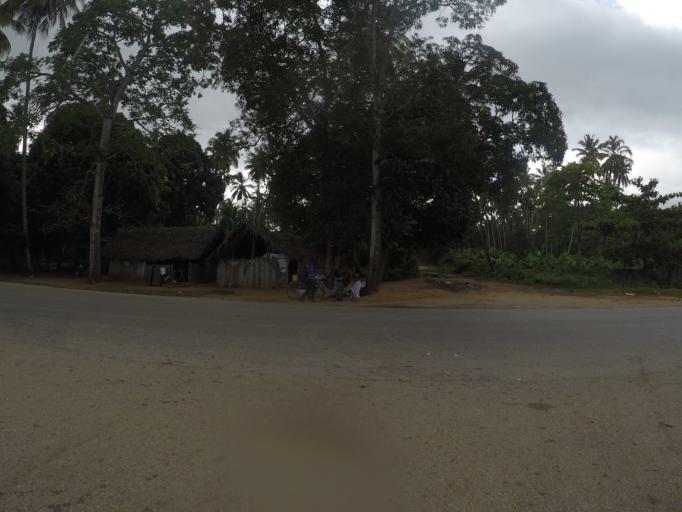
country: TZ
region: Zanzibar North
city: Mkokotoni
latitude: -5.9973
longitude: 39.1968
